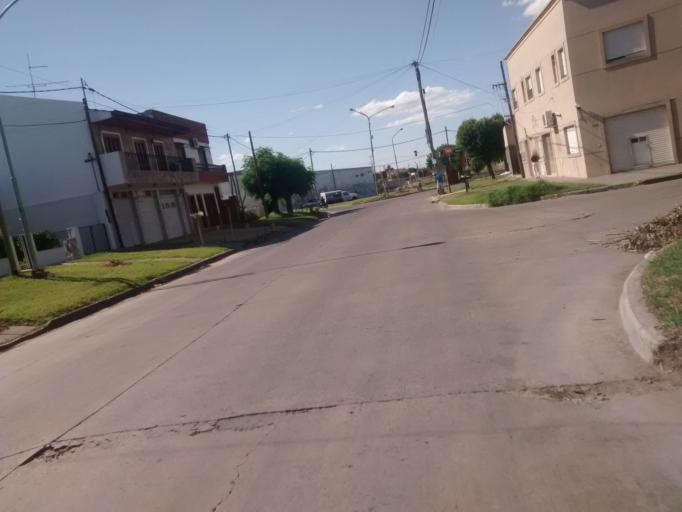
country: AR
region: Buenos Aires
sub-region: Partido de La Plata
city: La Plata
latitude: -34.9273
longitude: -57.9074
